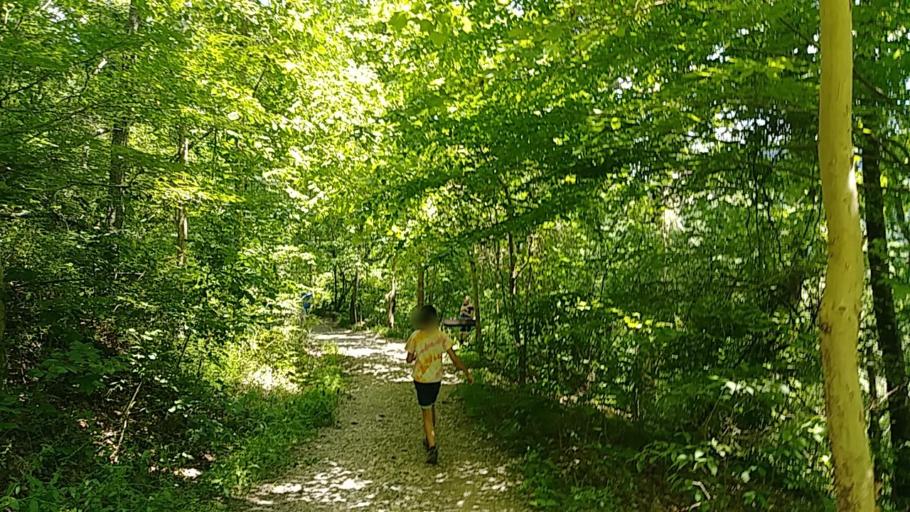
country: US
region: Tennessee
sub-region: Claiborne County
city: Harrogate
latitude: 36.6028
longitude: -83.6709
